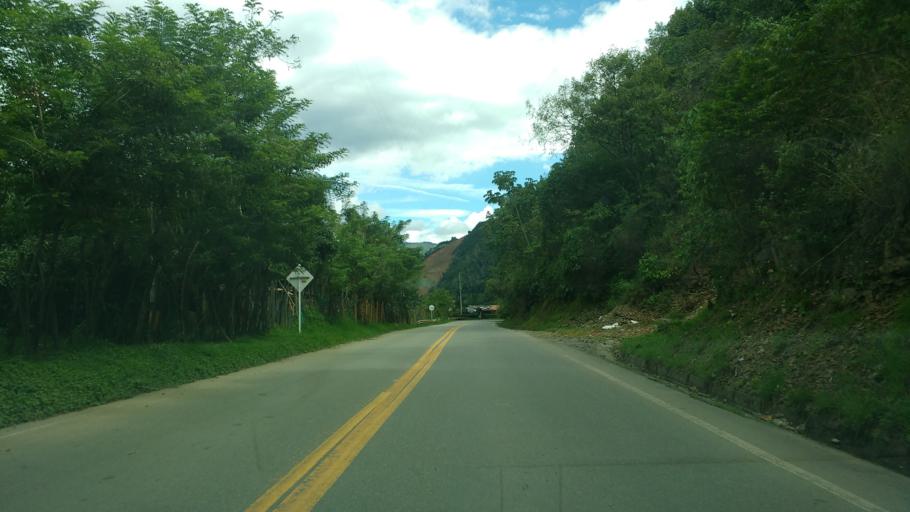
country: CO
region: Antioquia
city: Amaga
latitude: 6.0539
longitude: -75.7274
